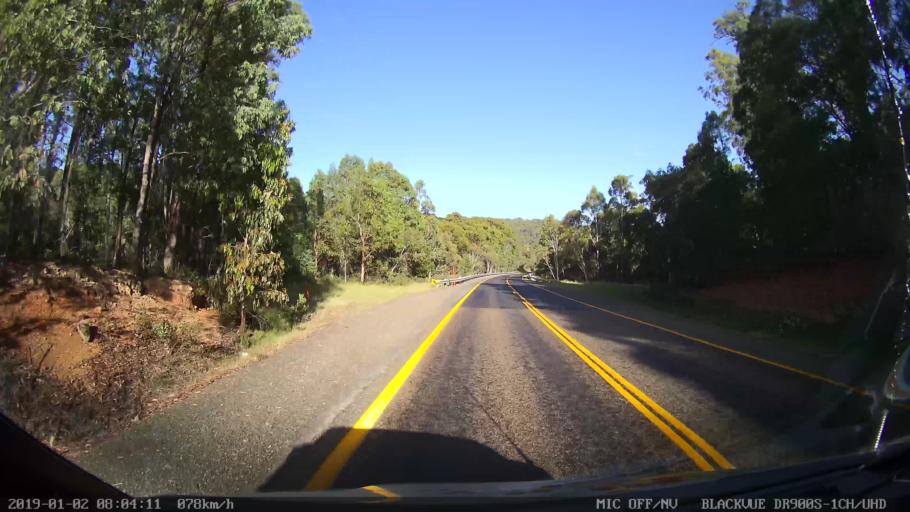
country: AU
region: New South Wales
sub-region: Tumut Shire
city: Tumut
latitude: -35.6631
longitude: 148.3982
